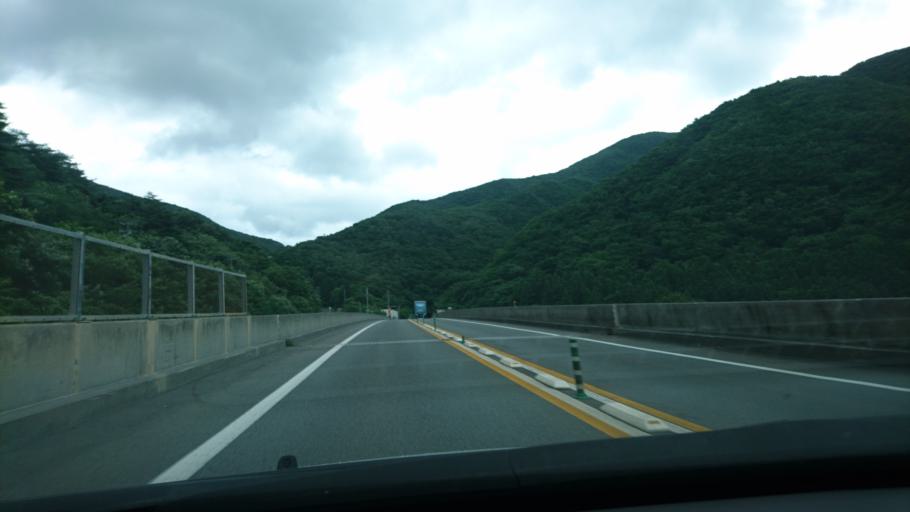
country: JP
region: Iwate
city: Ofunato
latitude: 39.1253
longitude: 141.7592
